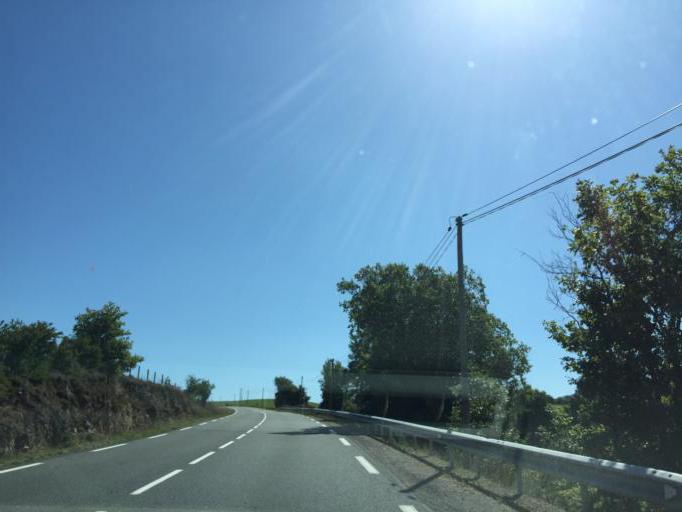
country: FR
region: Midi-Pyrenees
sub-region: Departement de l'Aveyron
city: Saint-Georges-de-Luzencon
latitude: 44.0138
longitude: 2.9913
